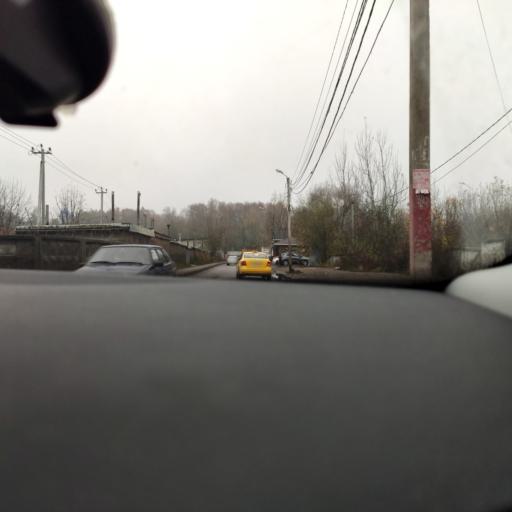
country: RU
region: Moskovskaya
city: Nakhabino
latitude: 55.8442
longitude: 37.1567
